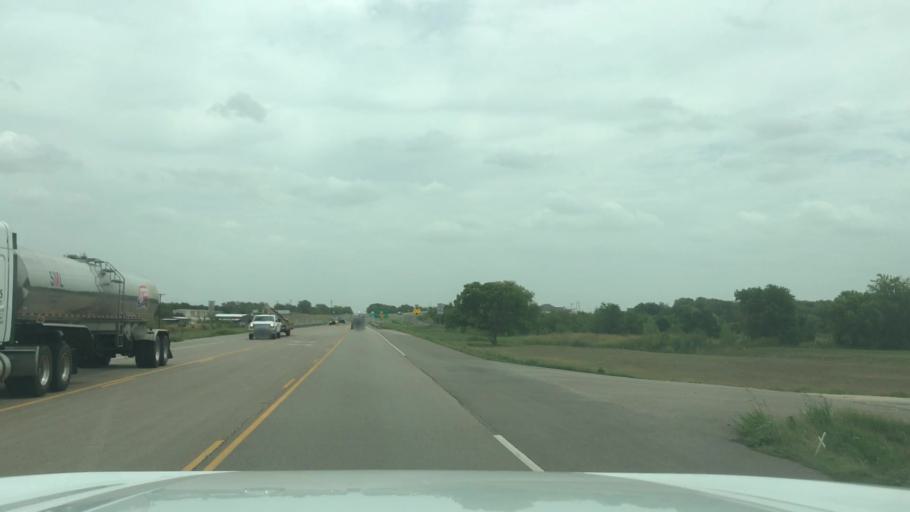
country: US
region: Texas
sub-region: McLennan County
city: Woodway
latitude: 31.5781
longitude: -97.2971
